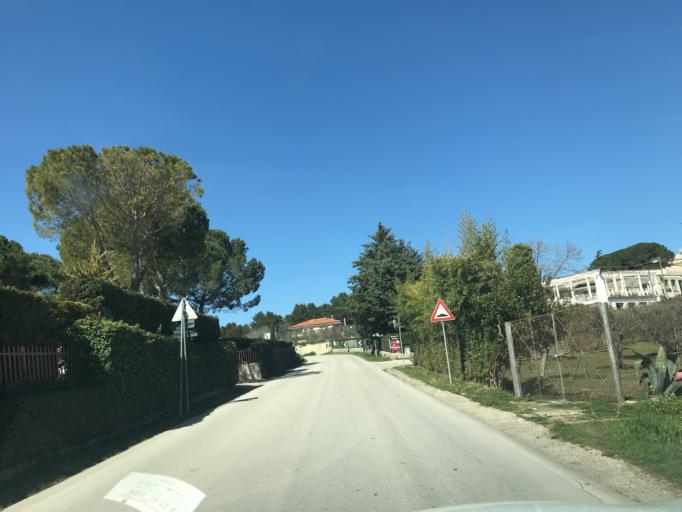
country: IT
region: Apulia
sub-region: Provincia di Bari
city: Gravina in Puglia
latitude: 40.8335
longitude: 16.4275
